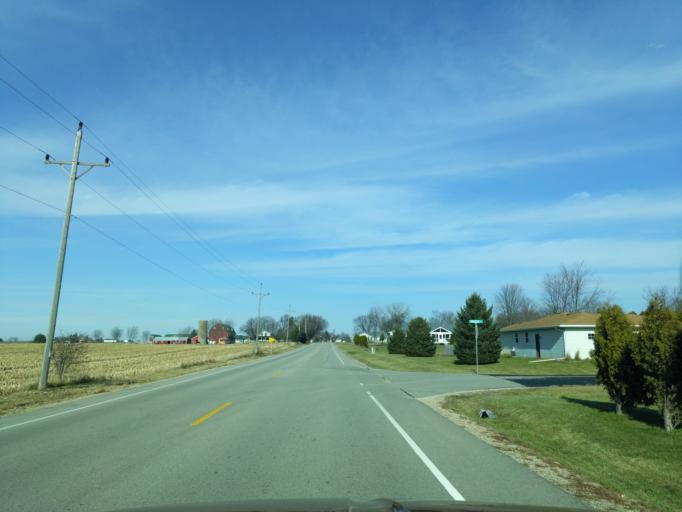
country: US
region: Wisconsin
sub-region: Walworth County
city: Elkhorn
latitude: 42.7244
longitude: -88.5820
